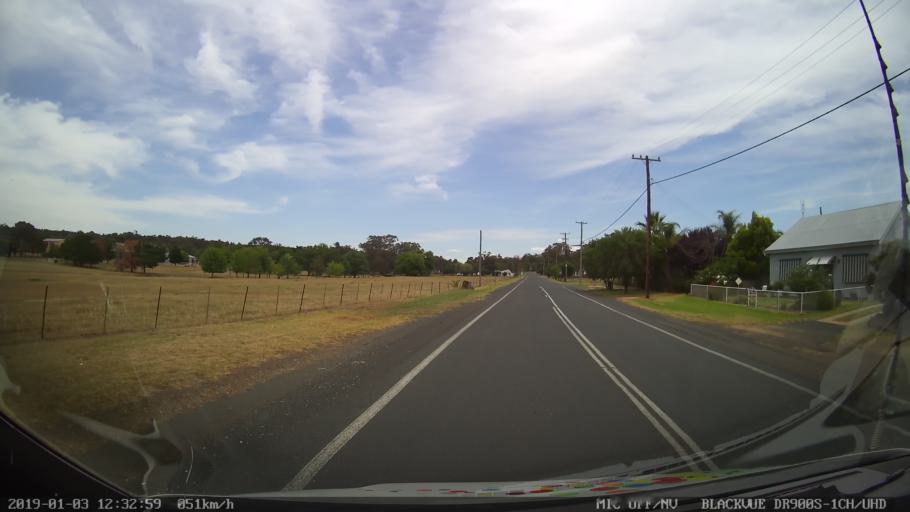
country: AU
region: New South Wales
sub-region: Weddin
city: Grenfell
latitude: -33.8887
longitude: 148.1623
